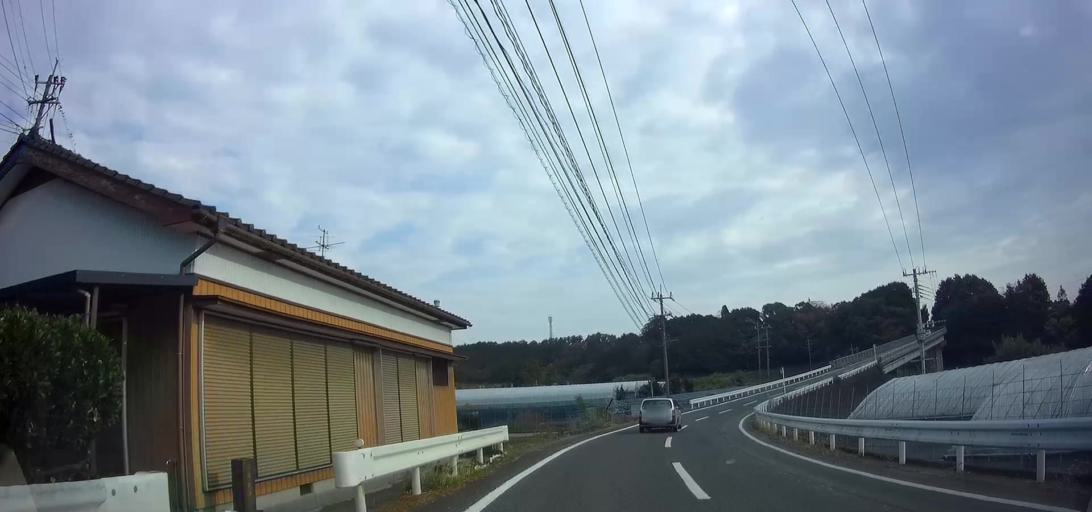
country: JP
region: Nagasaki
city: Shimabara
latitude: 32.6918
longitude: 130.2964
